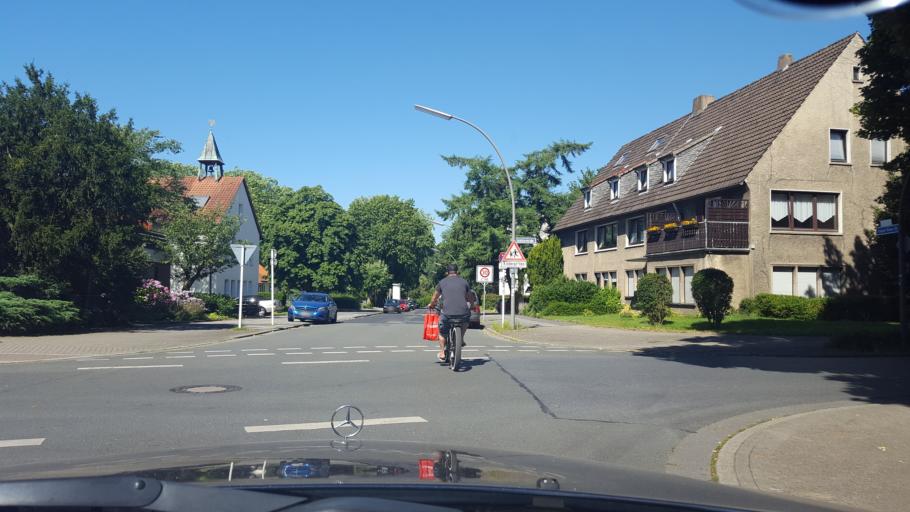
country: DE
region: North Rhine-Westphalia
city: Marl
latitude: 51.6492
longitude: 7.0816
